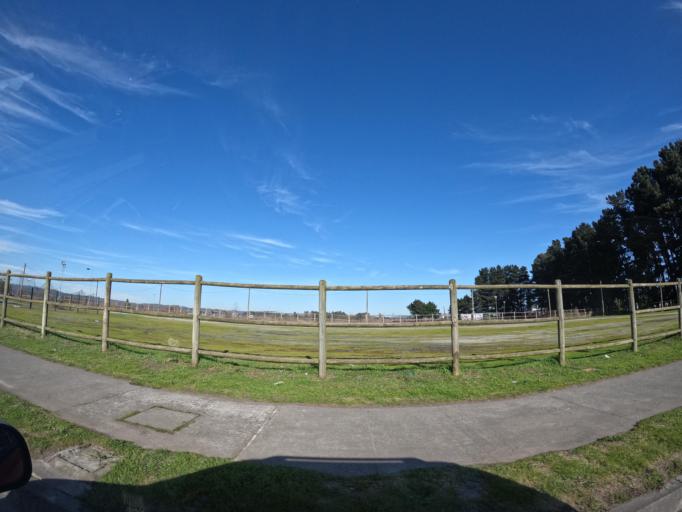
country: CL
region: Biobio
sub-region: Provincia de Concepcion
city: Concepcion
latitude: -36.7735
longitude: -73.0679
